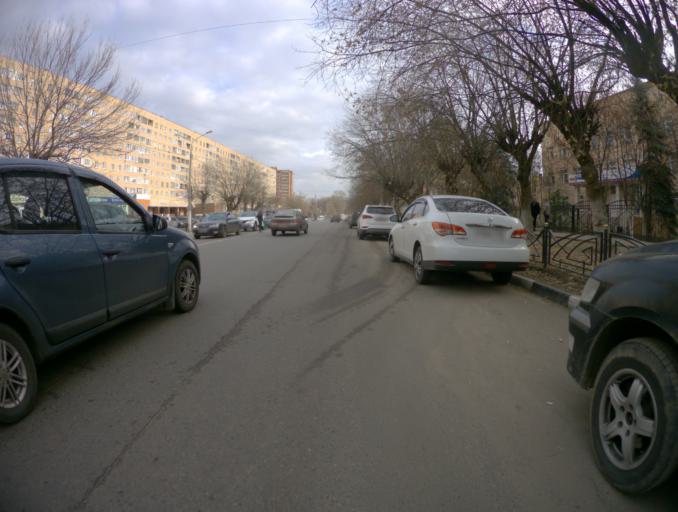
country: RU
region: Moskovskaya
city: Orekhovo-Zuyevo
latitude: 55.7977
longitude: 38.9759
